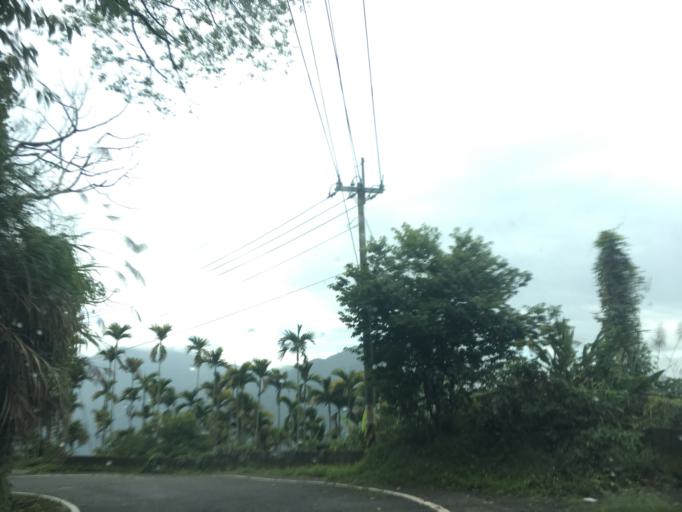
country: TW
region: Taiwan
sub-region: Yunlin
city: Douliu
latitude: 23.5625
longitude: 120.6203
